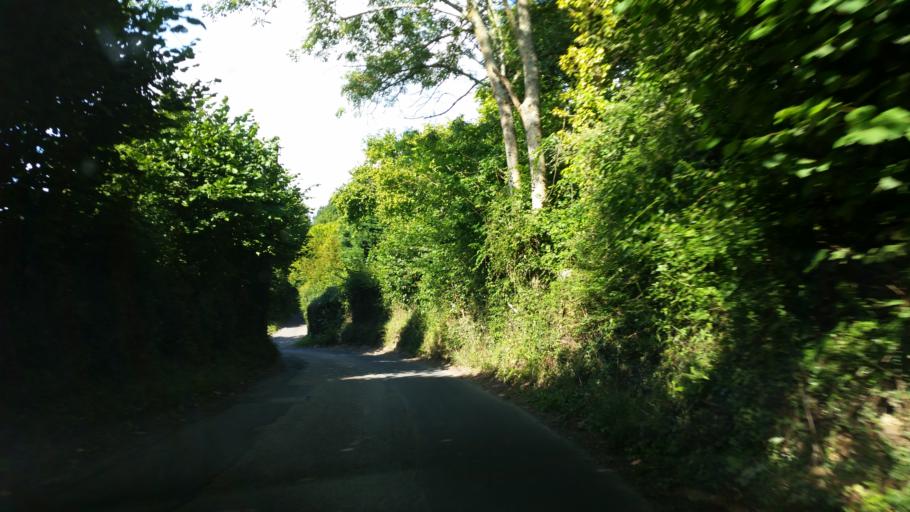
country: FR
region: Lower Normandy
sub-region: Departement du Calvados
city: Equemauville
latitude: 49.3985
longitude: 0.2245
